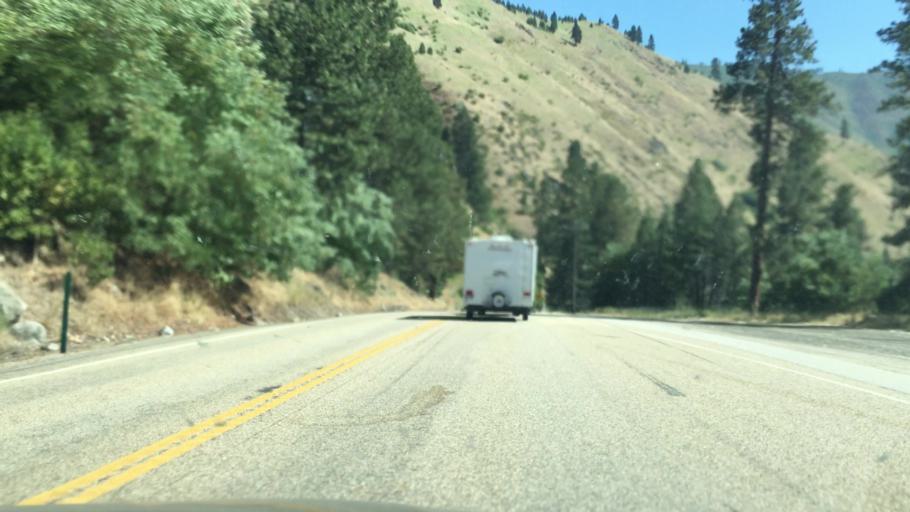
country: US
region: Idaho
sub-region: Boise County
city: Idaho City
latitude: 44.0474
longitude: -116.1315
